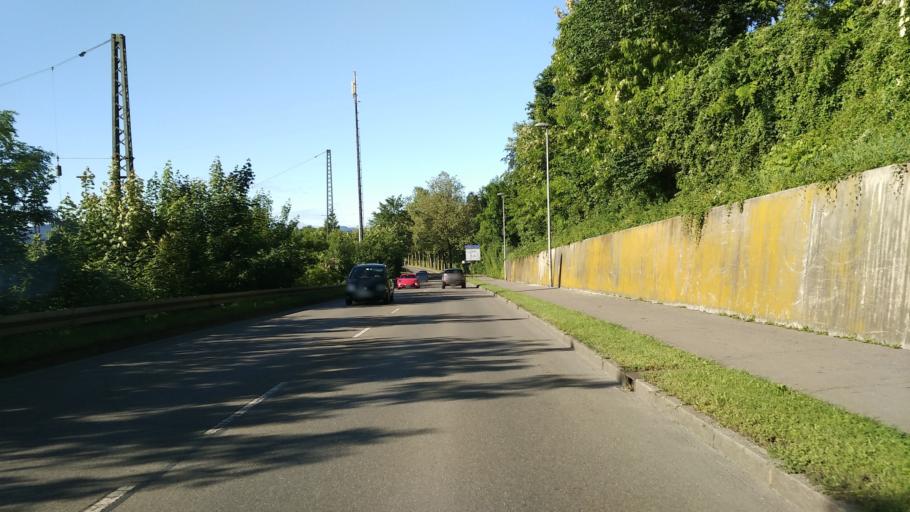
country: DE
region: Baden-Wuerttemberg
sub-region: Regierungsbezirk Stuttgart
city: Nurtingen
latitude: 48.6319
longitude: 9.3436
